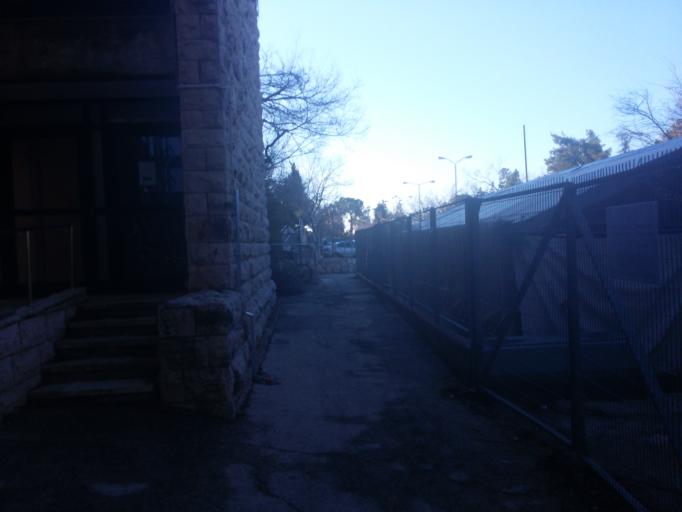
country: IL
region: Jerusalem
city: Jerusalem
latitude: 31.7781
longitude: 35.1957
